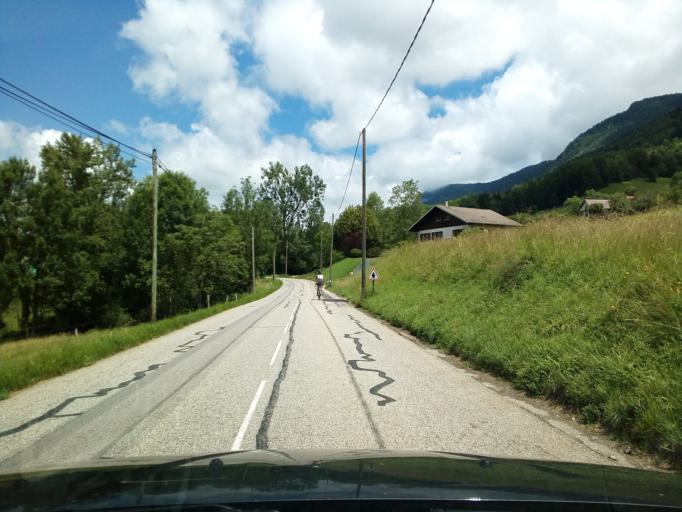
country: FR
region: Rhone-Alpes
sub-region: Departement de la Savoie
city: Les Echelles
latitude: 45.4734
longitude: 5.7617
